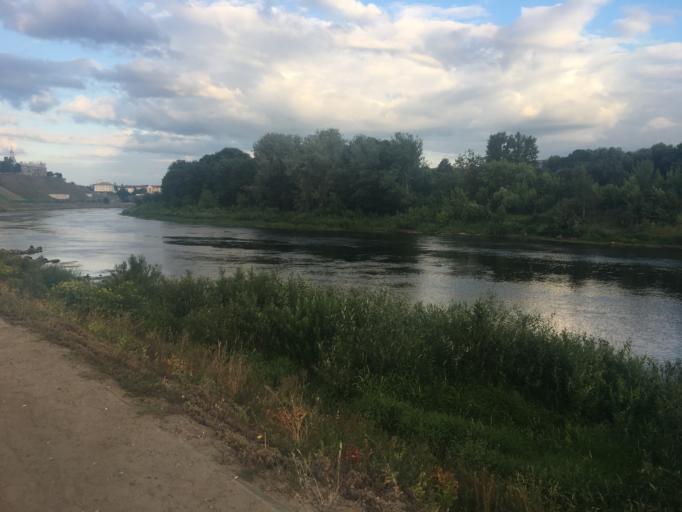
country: BY
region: Grodnenskaya
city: Hrodna
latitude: 53.6787
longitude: 23.8146
